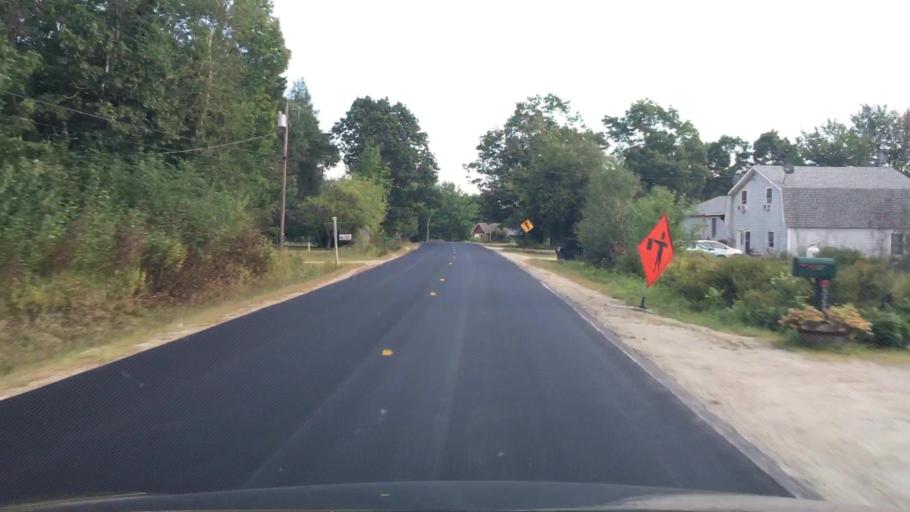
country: US
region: Maine
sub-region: Hancock County
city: Orland
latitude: 44.5472
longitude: -68.6205
